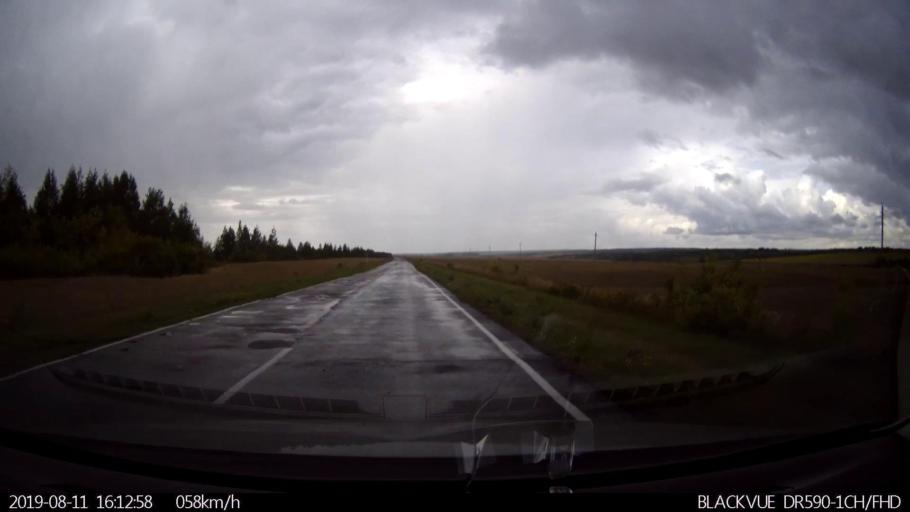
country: RU
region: Ulyanovsk
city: Ignatovka
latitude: 54.0162
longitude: 47.6386
